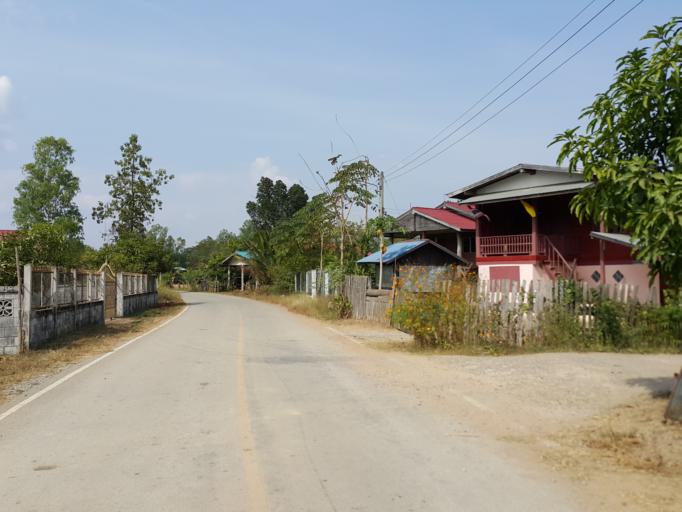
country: TH
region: Sukhothai
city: Thung Saliam
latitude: 17.3274
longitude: 99.4408
